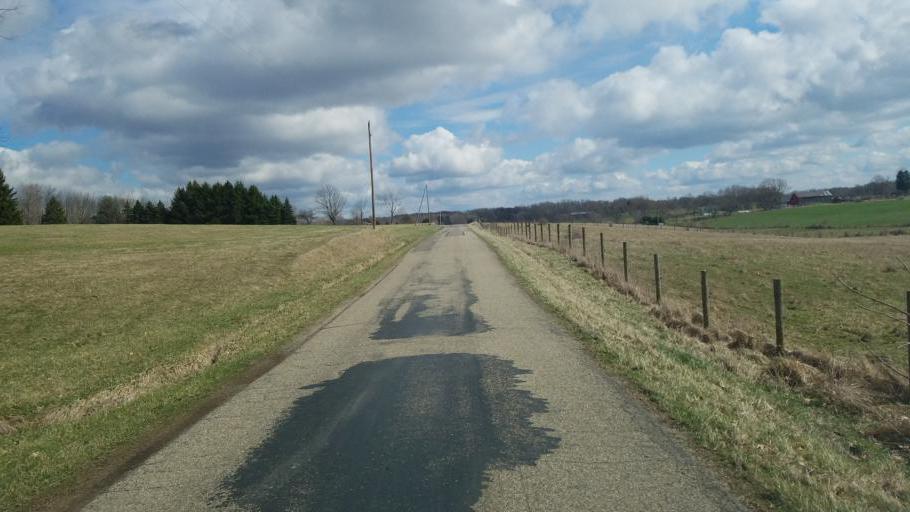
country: US
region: Ohio
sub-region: Sandusky County
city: Bellville
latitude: 40.5504
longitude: -82.5159
